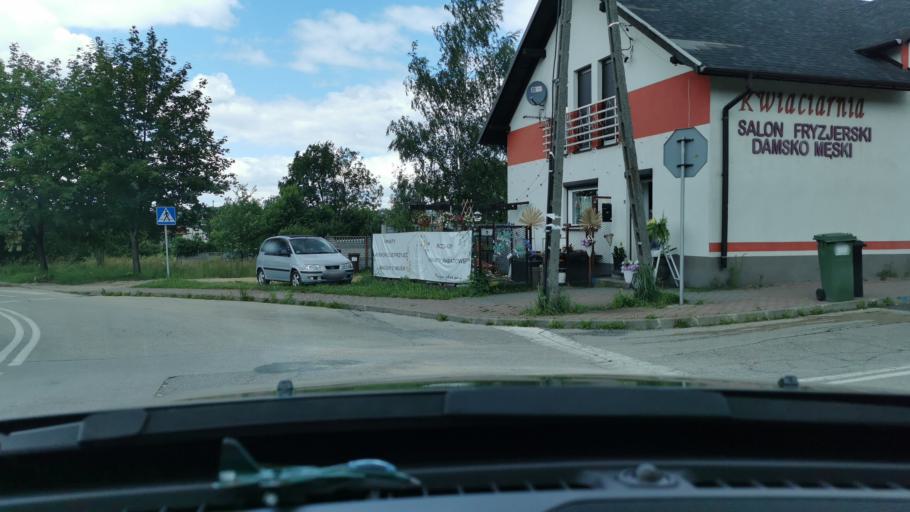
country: PL
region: Lesser Poland Voivodeship
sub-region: Powiat chrzanowski
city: Chrzanow
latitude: 50.1328
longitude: 19.4135
